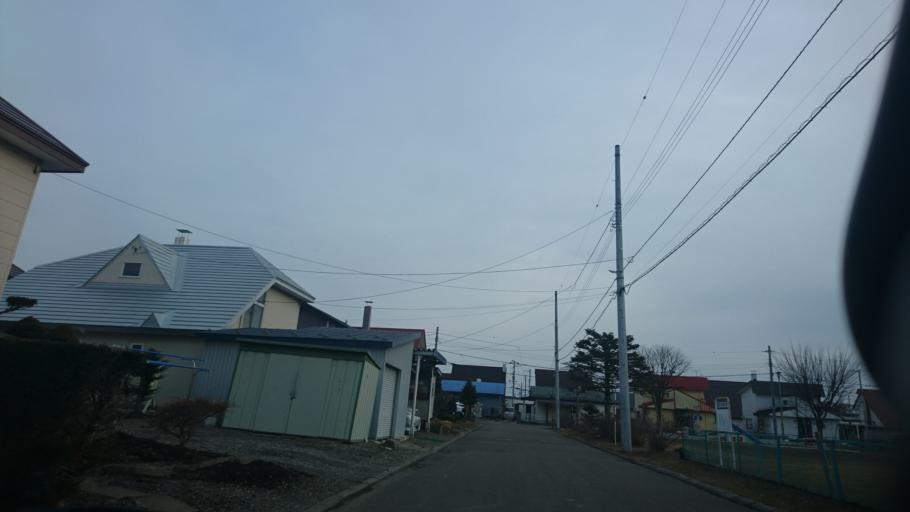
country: JP
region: Hokkaido
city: Otofuke
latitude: 42.9941
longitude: 143.1911
